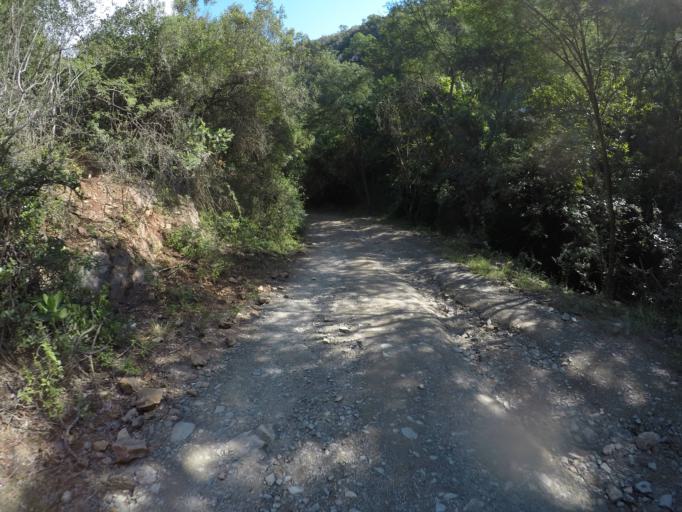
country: ZA
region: Eastern Cape
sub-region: Cacadu District Municipality
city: Kareedouw
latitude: -33.6450
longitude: 24.4521
